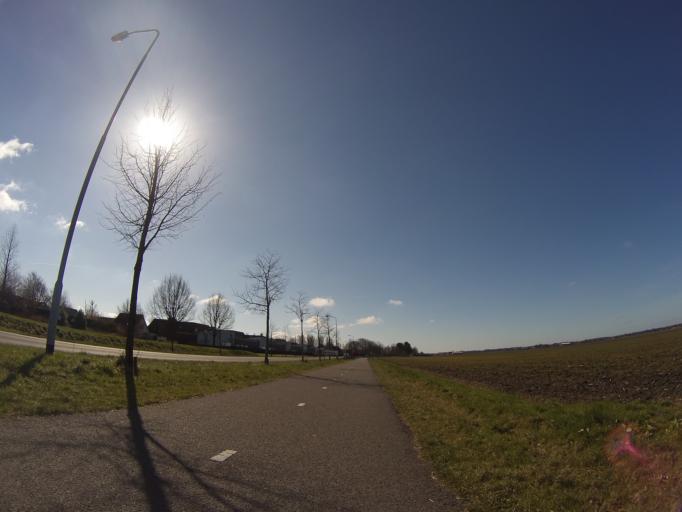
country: NL
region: Drenthe
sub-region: Gemeente Emmen
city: Emmen
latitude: 52.7403
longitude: 6.8764
